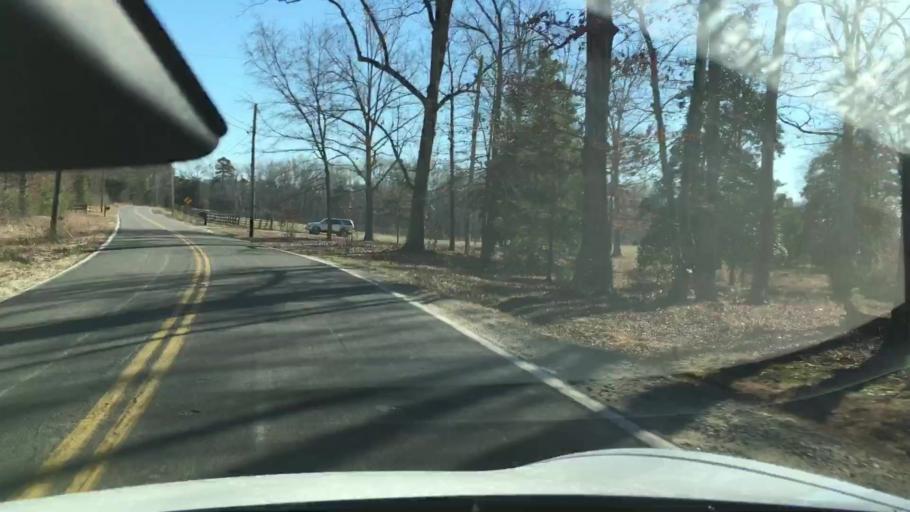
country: US
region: Virginia
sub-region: Henrico County
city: Short Pump
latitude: 37.5876
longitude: -77.7536
